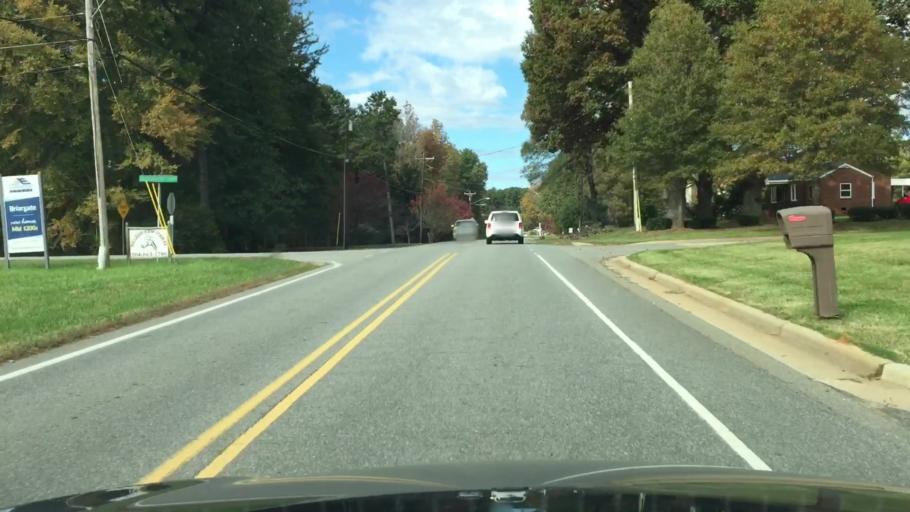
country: US
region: North Carolina
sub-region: Iredell County
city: Mooresville
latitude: 35.5518
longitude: -80.8095
